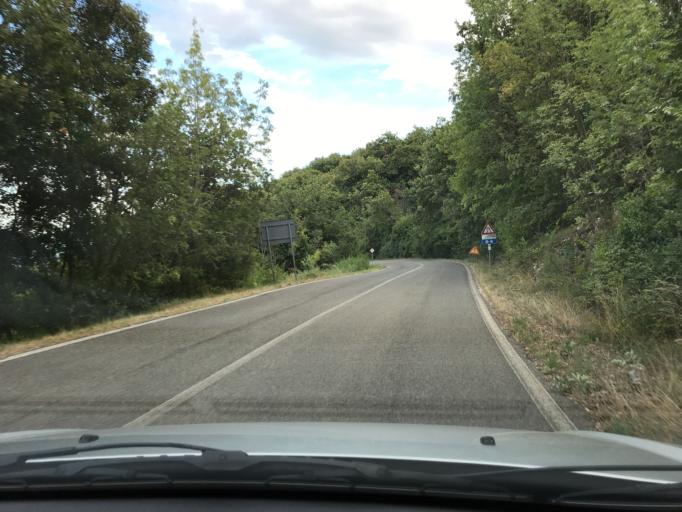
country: IT
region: Umbria
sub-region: Provincia di Terni
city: Guardea
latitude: 42.6559
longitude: 12.3483
